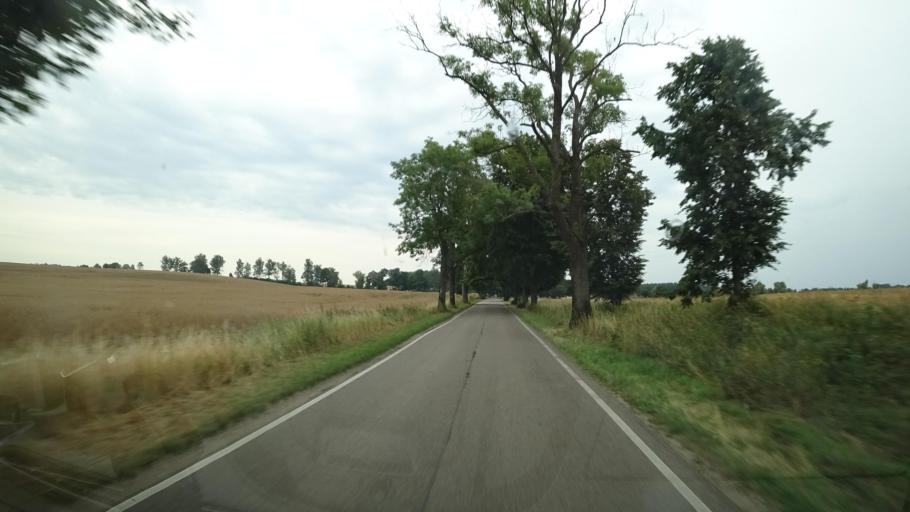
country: PL
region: Warmian-Masurian Voivodeship
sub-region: Powiat gizycki
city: Ryn
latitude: 53.9025
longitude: 21.5667
